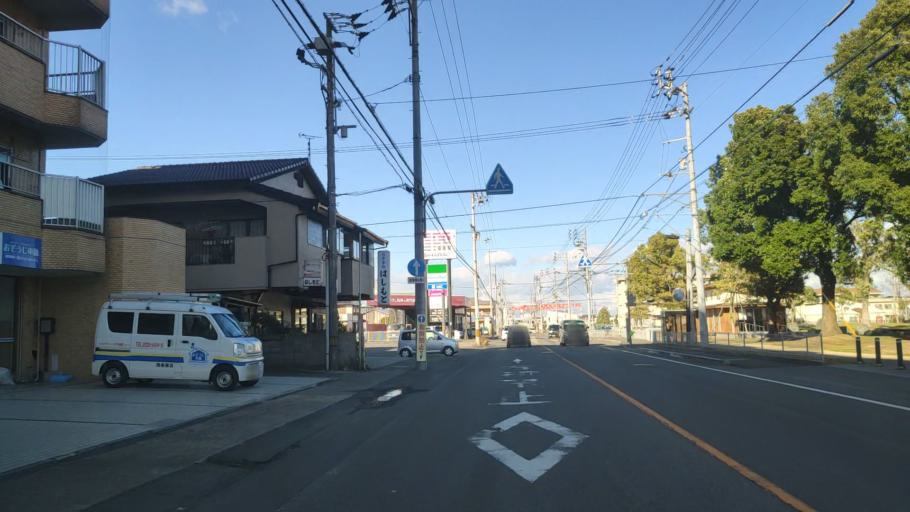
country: JP
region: Ehime
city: Saijo
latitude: 33.9170
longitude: 133.1919
